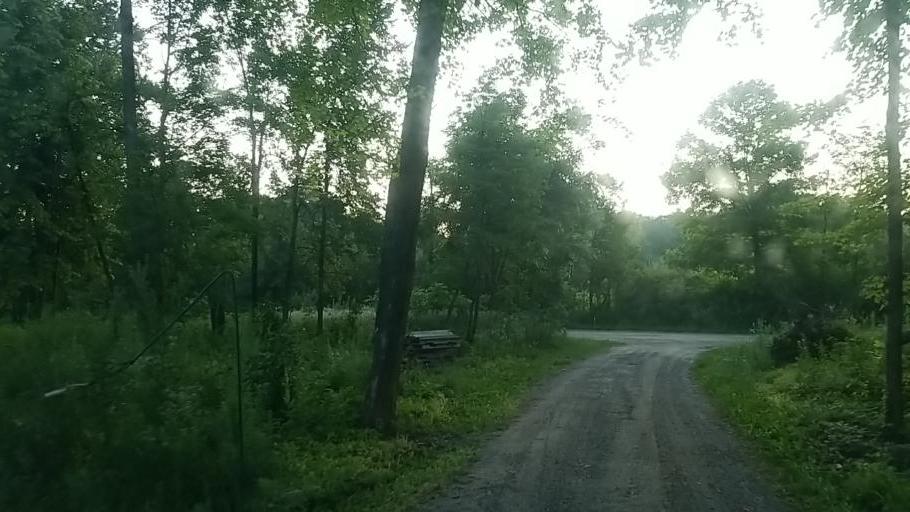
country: US
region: Michigan
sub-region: Osceola County
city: Evart
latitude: 43.9067
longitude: -85.2070
